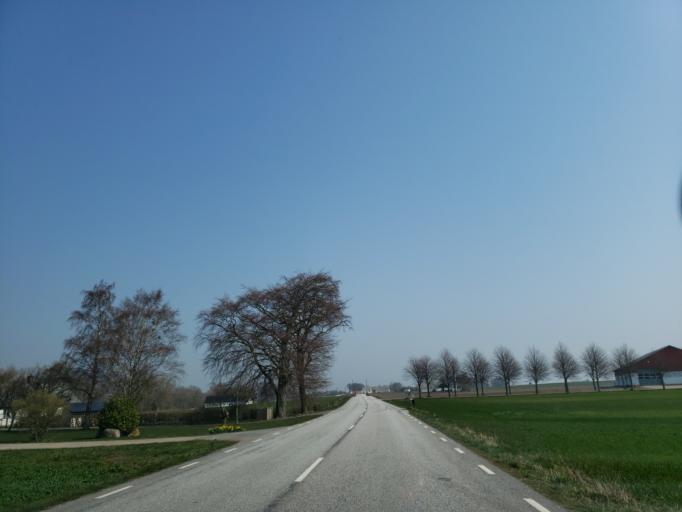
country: SE
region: Skane
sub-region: Simrishamns Kommun
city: Simrishamn
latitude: 55.4684
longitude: 14.2164
